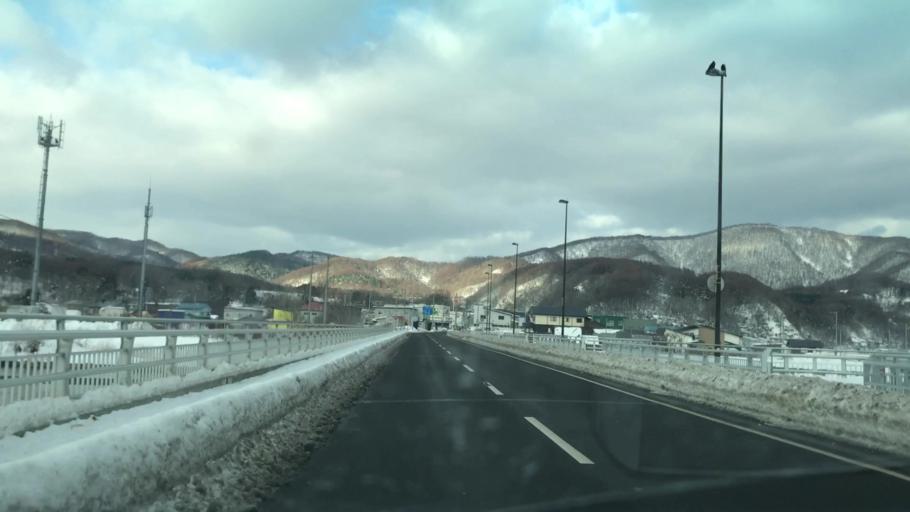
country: JP
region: Hokkaido
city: Yoichi
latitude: 43.2621
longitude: 140.6463
